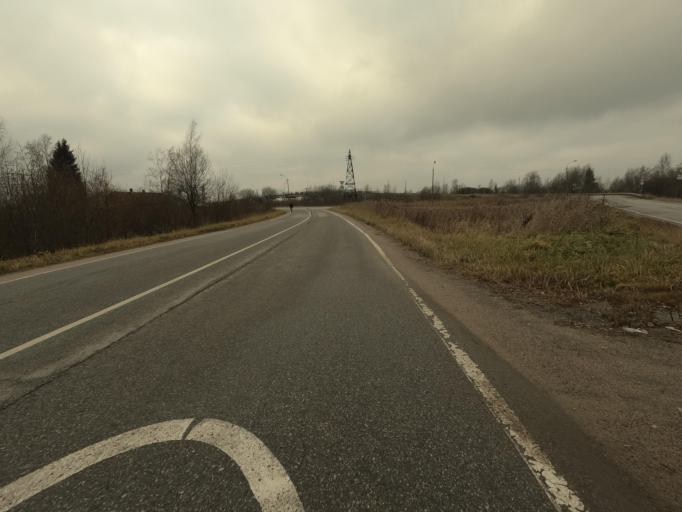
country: RU
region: Leningrad
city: Lyuban'
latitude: 59.4857
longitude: 31.2656
